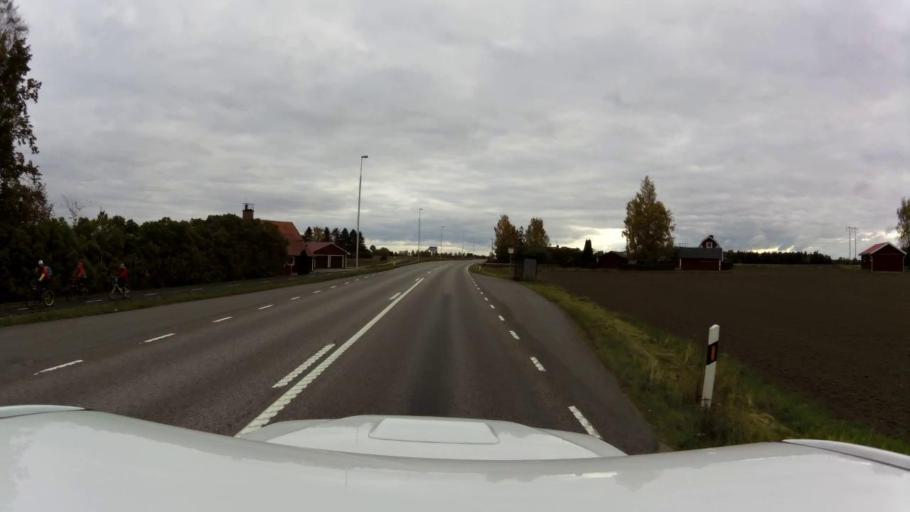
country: SE
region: OEstergoetland
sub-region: Linkopings Kommun
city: Berg
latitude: 58.4518
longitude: 15.5561
